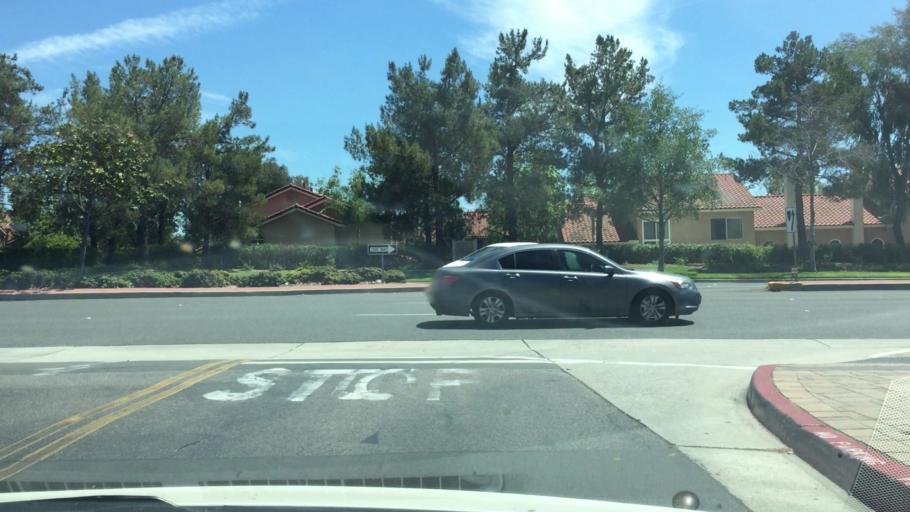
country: US
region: California
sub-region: Orange County
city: Trabuco Canyon
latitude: 33.6491
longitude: -117.5829
